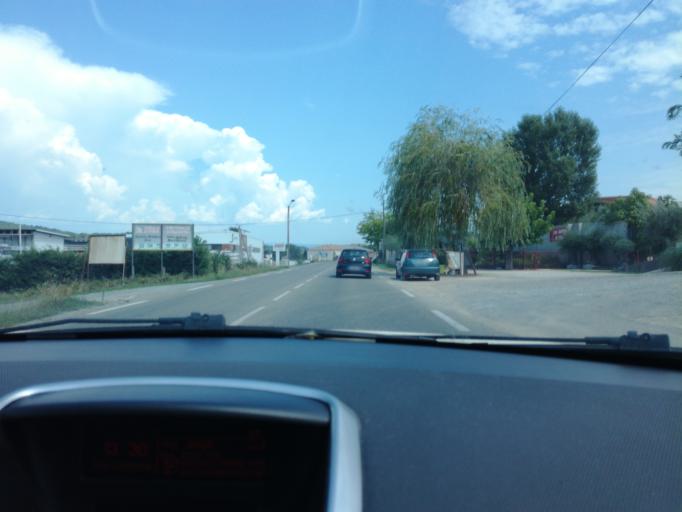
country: FR
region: Rhone-Alpes
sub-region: Departement de l'Ardeche
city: Ruoms
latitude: 44.4667
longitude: 4.3472
